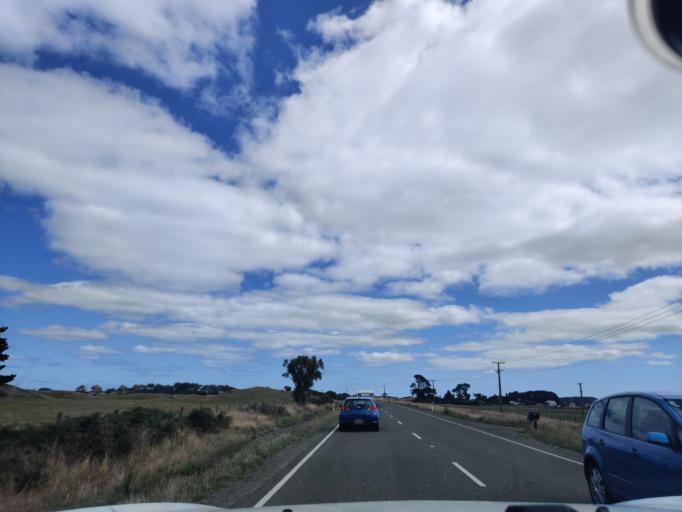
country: NZ
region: Manawatu-Wanganui
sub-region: Horowhenua District
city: Foxton
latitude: -40.4165
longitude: 175.4055
